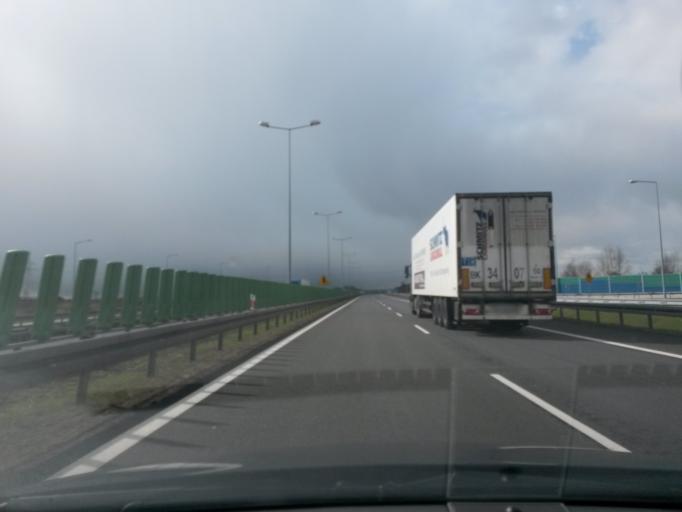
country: PL
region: Greater Poland Voivodeship
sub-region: Powiat koninski
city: Stare Miasto
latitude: 52.1632
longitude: 18.2054
